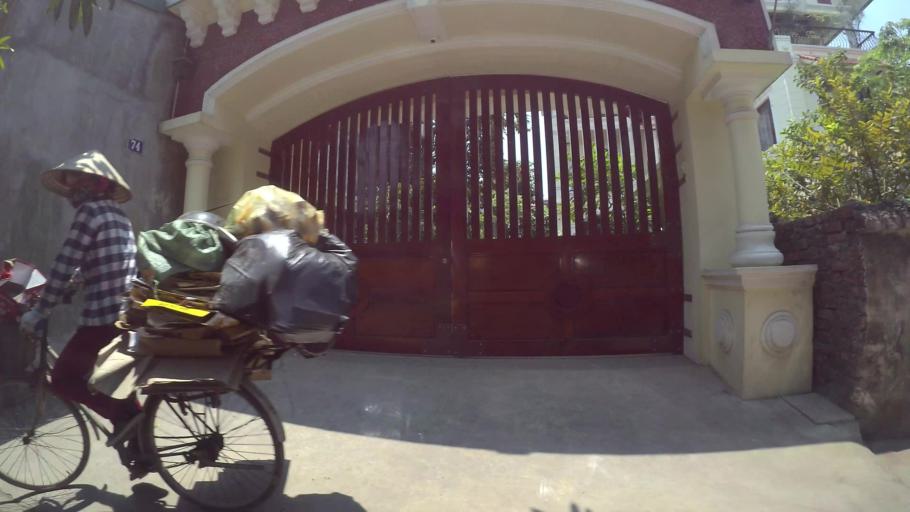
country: VN
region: Ha Noi
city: Hoan Kiem
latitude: 21.0268
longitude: 105.8866
